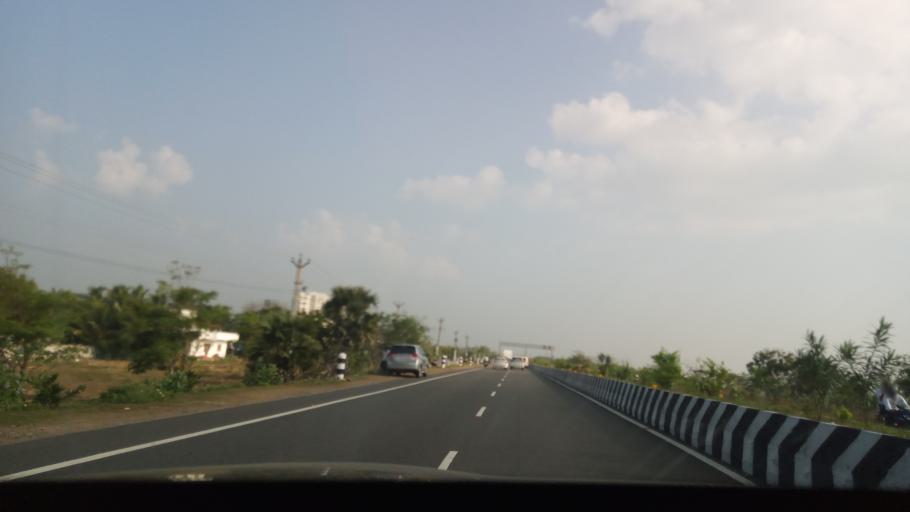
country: IN
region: Tamil Nadu
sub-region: Kancheepuram
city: Injambakkam
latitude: 12.7671
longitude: 80.2468
